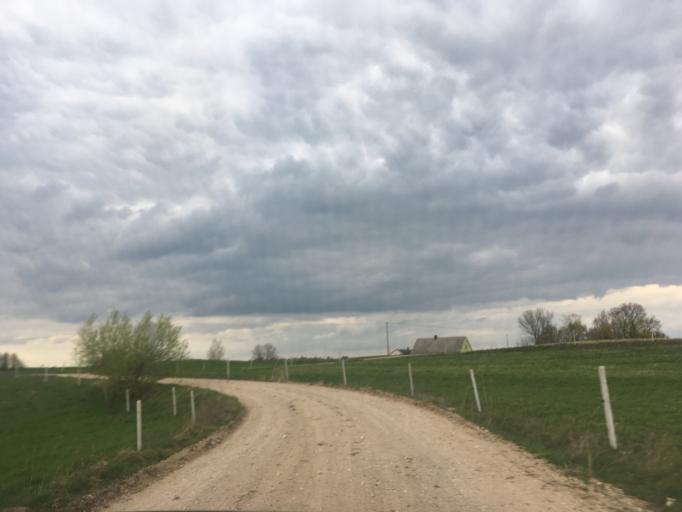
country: PL
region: Podlasie
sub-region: Powiat sejnenski
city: Punsk
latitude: 54.2872
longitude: 23.1026
